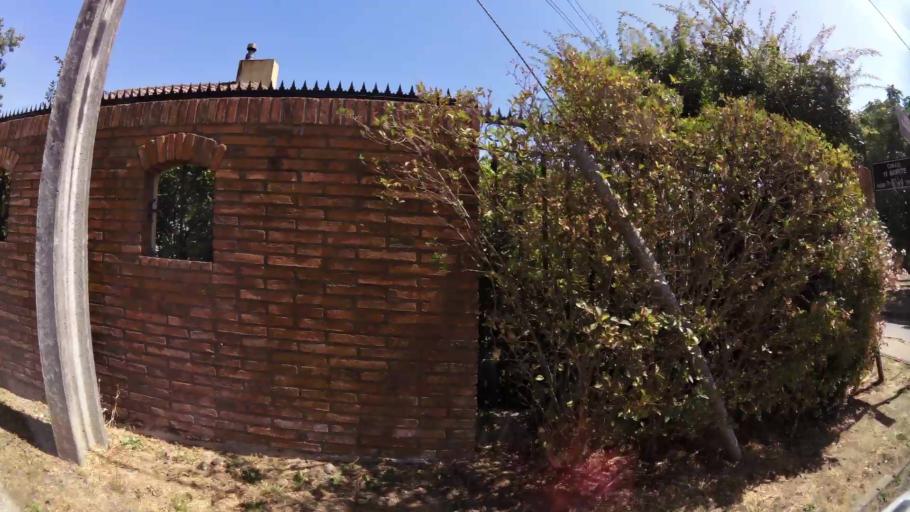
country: CL
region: Maule
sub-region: Provincia de Talca
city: Talca
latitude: -35.4220
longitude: -71.6297
